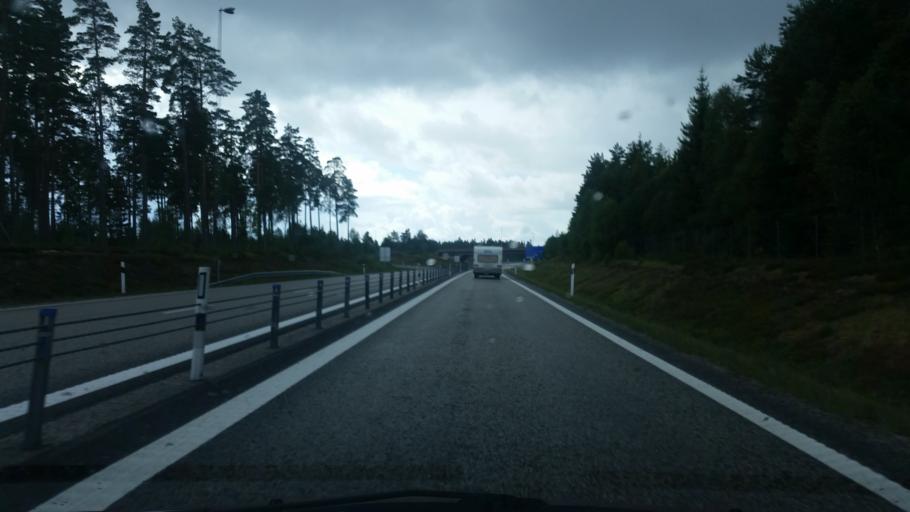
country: SE
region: Joenkoeping
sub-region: Gislaveds Kommun
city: Gislaved
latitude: 57.3271
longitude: 13.5458
